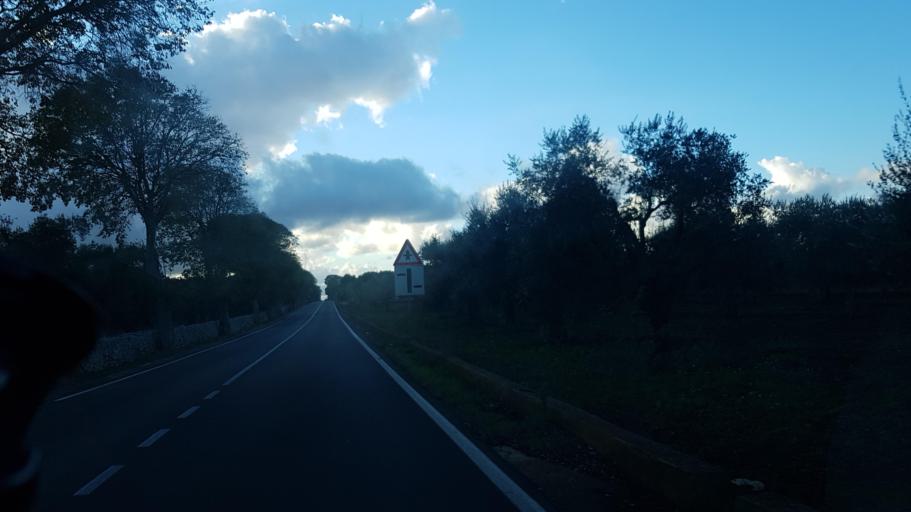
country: IT
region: Apulia
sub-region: Provincia di Brindisi
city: San Michele Salentino
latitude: 40.6465
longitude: 17.6181
